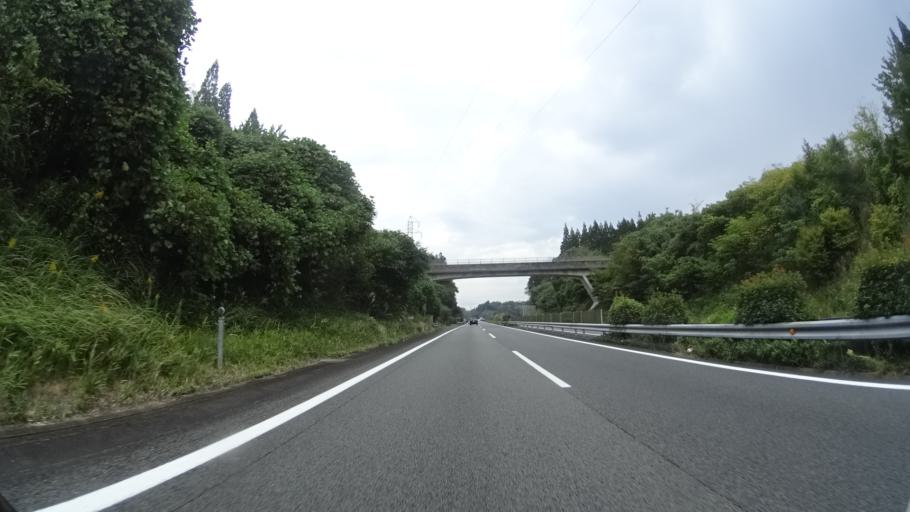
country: JP
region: Kumamoto
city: Hitoyoshi
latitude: 32.2110
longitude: 130.7742
